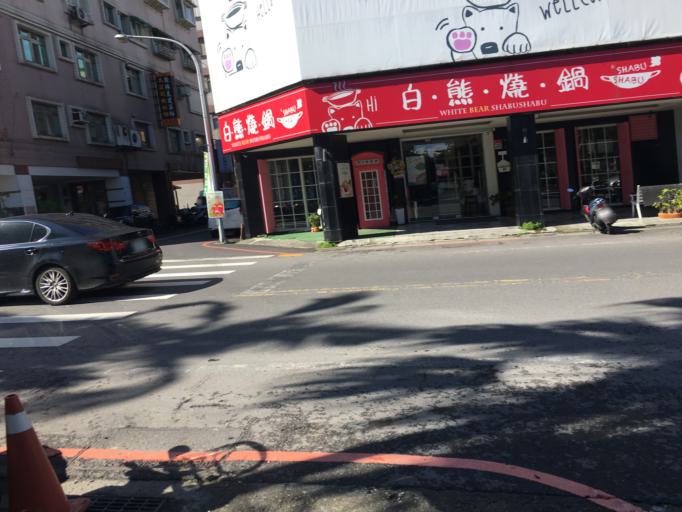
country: TW
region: Taiwan
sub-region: Yilan
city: Yilan
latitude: 24.6842
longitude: 121.7712
